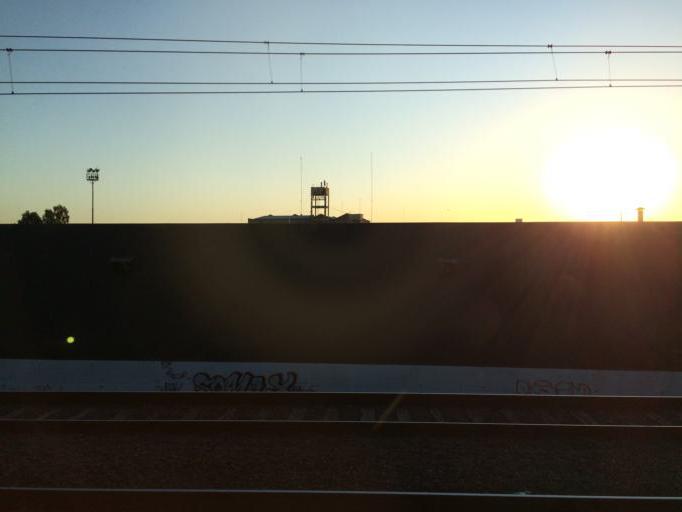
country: AR
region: Buenos Aires
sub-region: Partido de Avellaneda
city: Avellaneda
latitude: -34.6556
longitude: -58.3783
